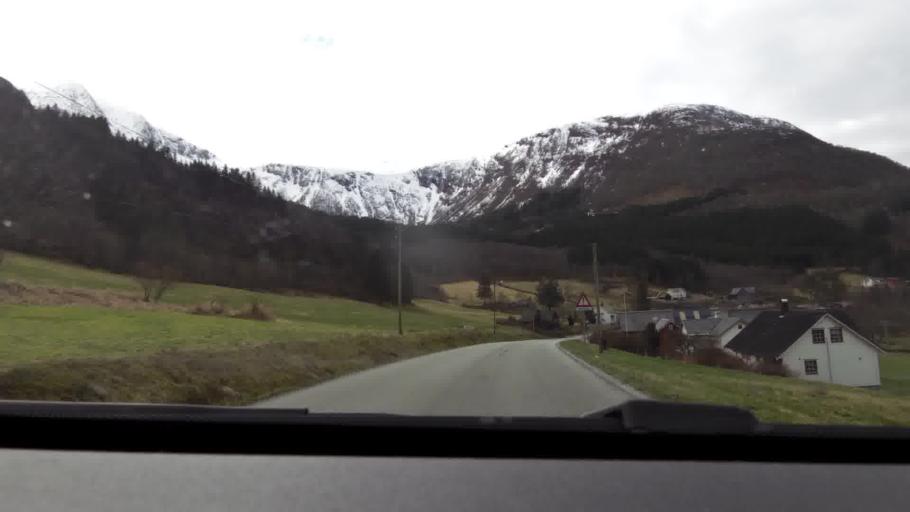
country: NO
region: More og Romsdal
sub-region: Gjemnes
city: Batnfjordsora
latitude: 62.9269
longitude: 7.5971
